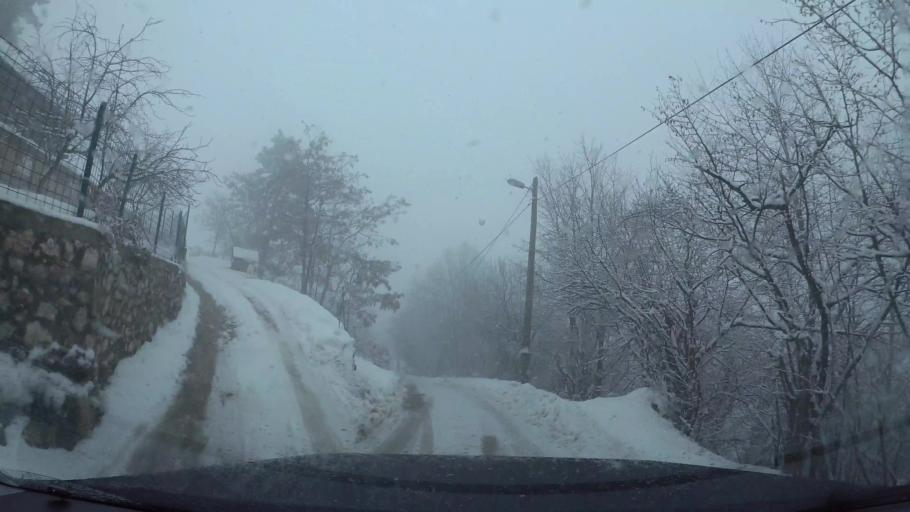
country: BA
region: Federation of Bosnia and Herzegovina
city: Kobilja Glava
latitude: 43.8488
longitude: 18.4456
